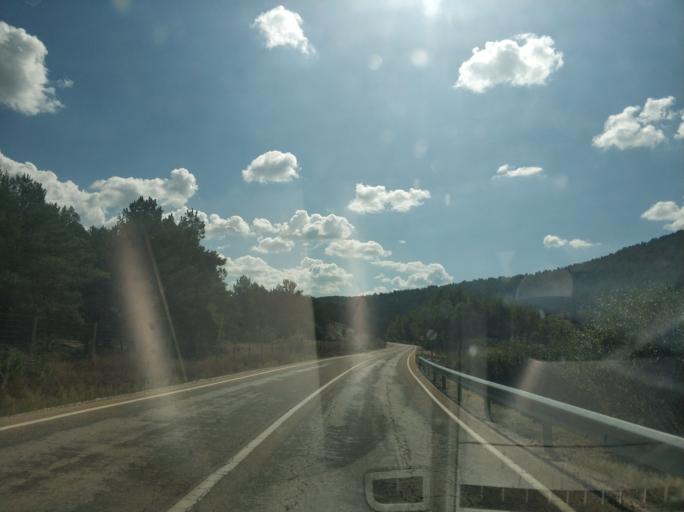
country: ES
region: Castille and Leon
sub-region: Provincia de Soria
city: San Leonardo de Yague
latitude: 41.8197
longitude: -3.0688
